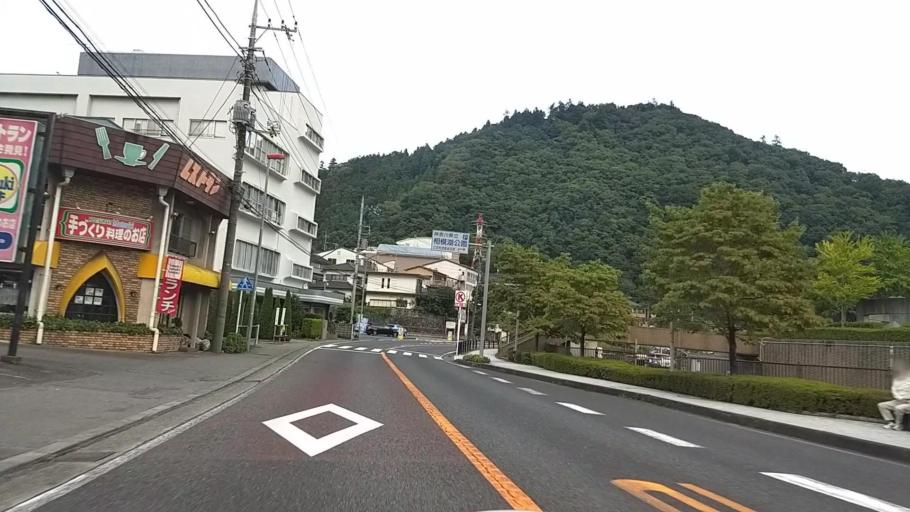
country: JP
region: Yamanashi
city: Uenohara
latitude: 35.6133
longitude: 139.1909
